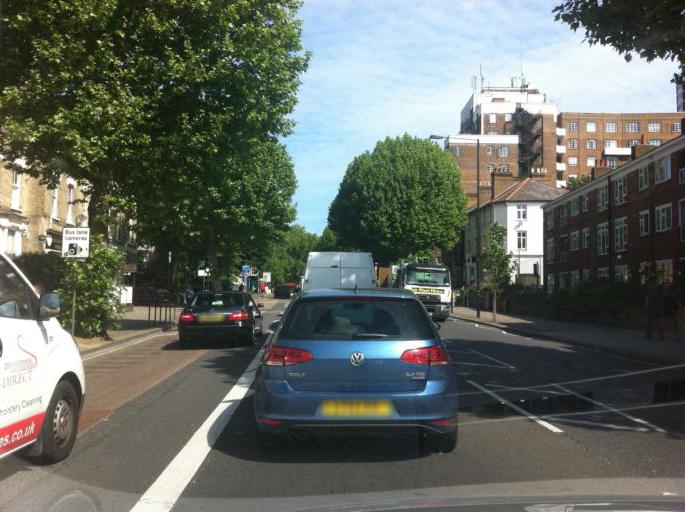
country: GB
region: England
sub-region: Greater London
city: Hammersmith
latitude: 51.5015
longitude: -0.2221
